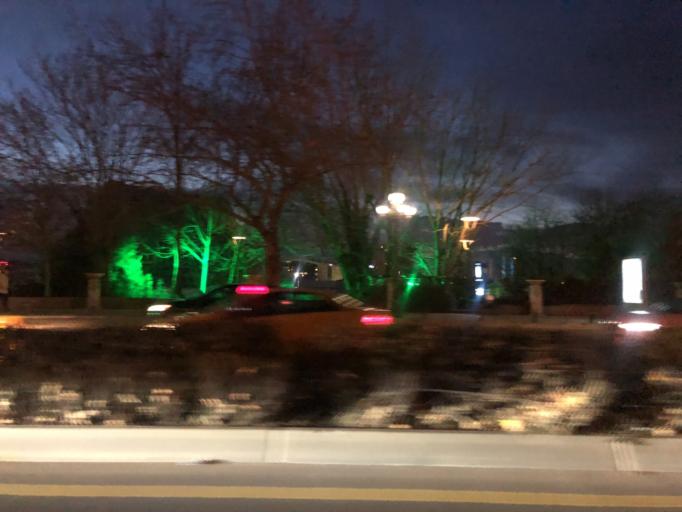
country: TR
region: Ankara
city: Ankara
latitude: 39.9332
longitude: 32.8531
